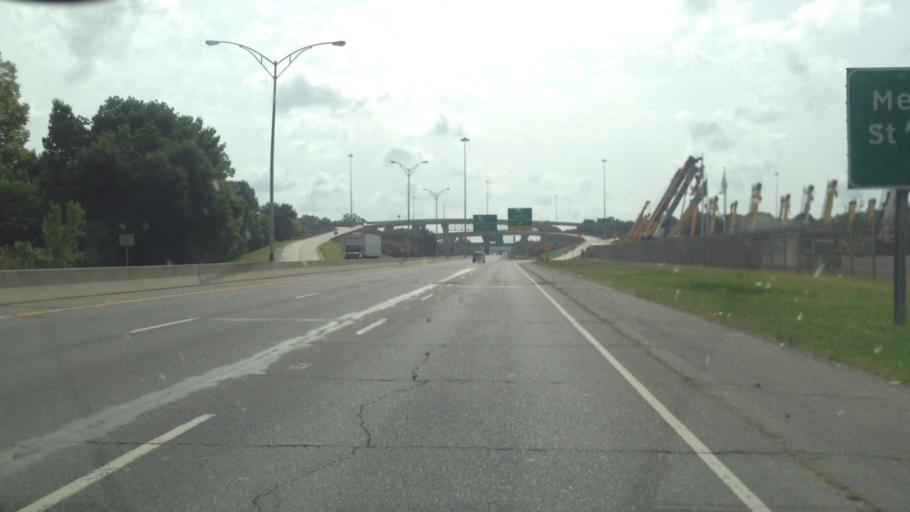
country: US
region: Louisiana
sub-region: East Baton Rouge Parish
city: Merrydale
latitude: 30.5086
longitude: -91.1649
